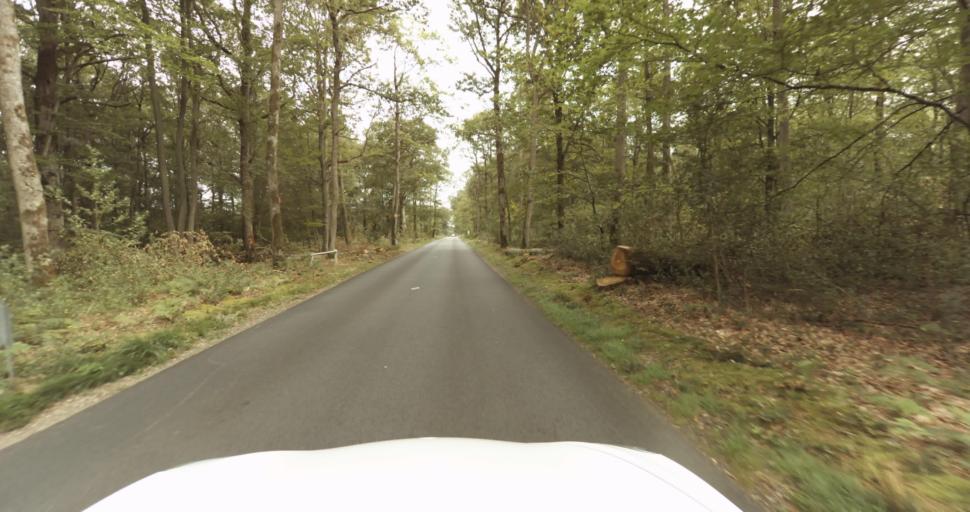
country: FR
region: Haute-Normandie
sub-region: Departement de l'Eure
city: Arnieres-sur-Iton
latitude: 48.9783
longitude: 1.0788
